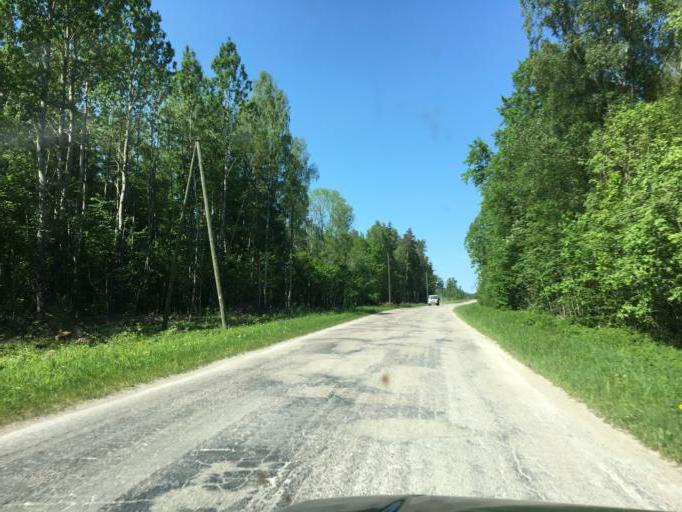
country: LV
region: Dundaga
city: Dundaga
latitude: 57.4539
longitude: 22.3214
